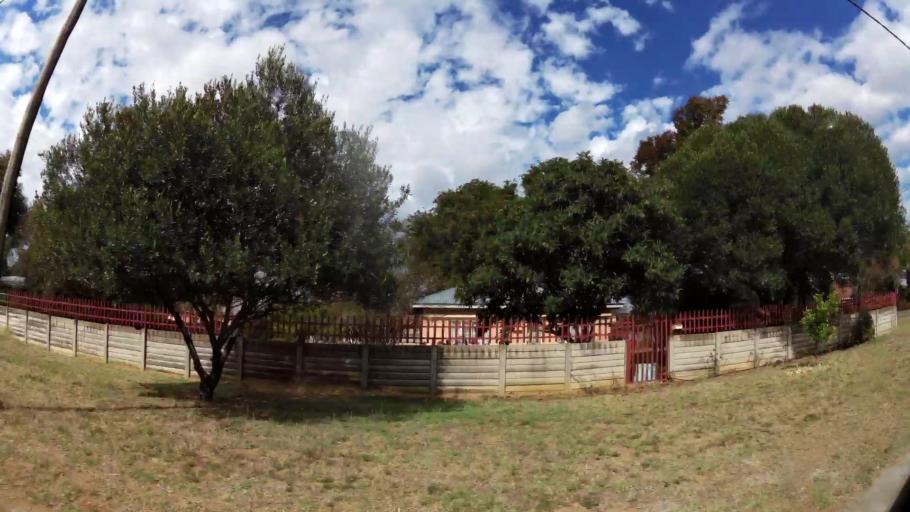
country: ZA
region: Limpopo
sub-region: Waterberg District Municipality
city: Modimolle
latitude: -24.7096
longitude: 28.4078
